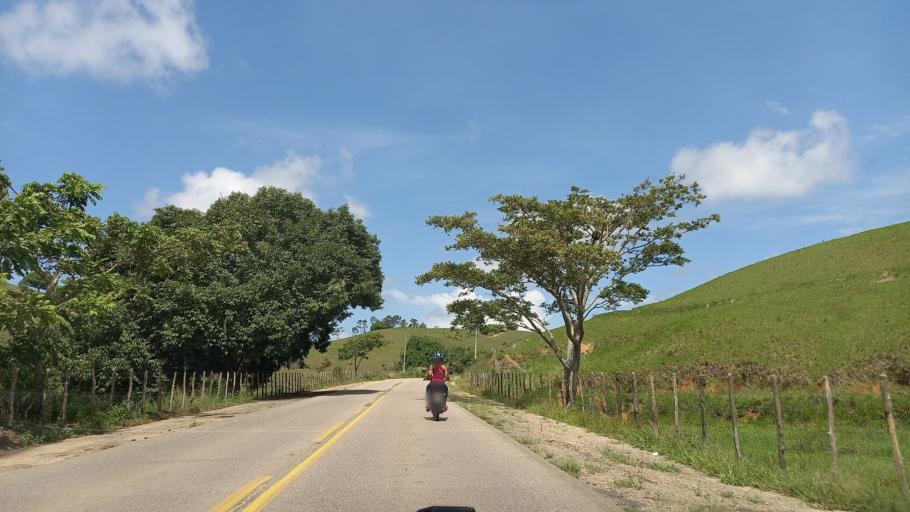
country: BR
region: Pernambuco
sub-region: Tamandare
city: Tamandare
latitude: -8.7448
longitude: -35.1724
